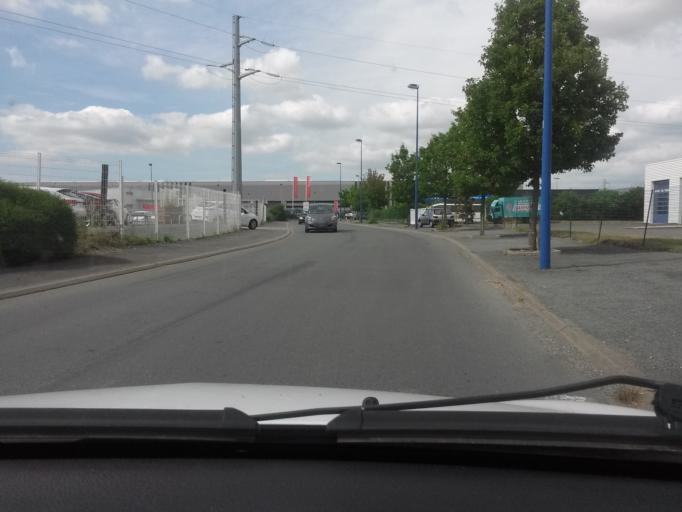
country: FR
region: Pays de la Loire
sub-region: Departement de la Vendee
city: Mouilleron-le-Captif
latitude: 46.7134
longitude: -1.4272
